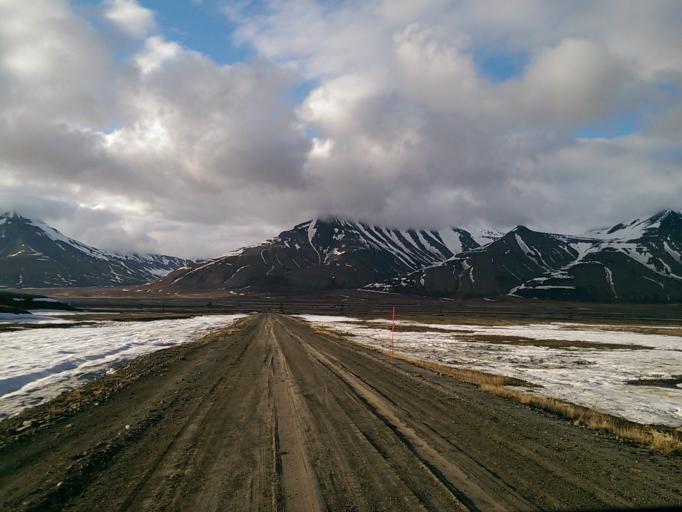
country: SJ
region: Svalbard
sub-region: Spitsbergen
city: Longyearbyen
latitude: 78.1905
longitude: 15.7891
